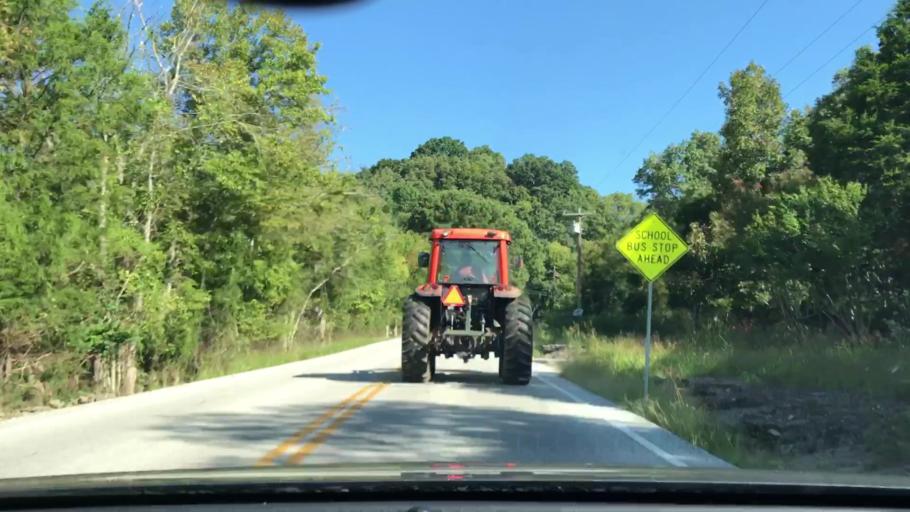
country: US
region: Tennessee
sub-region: Smith County
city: Carthage
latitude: 36.2955
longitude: -85.9541
